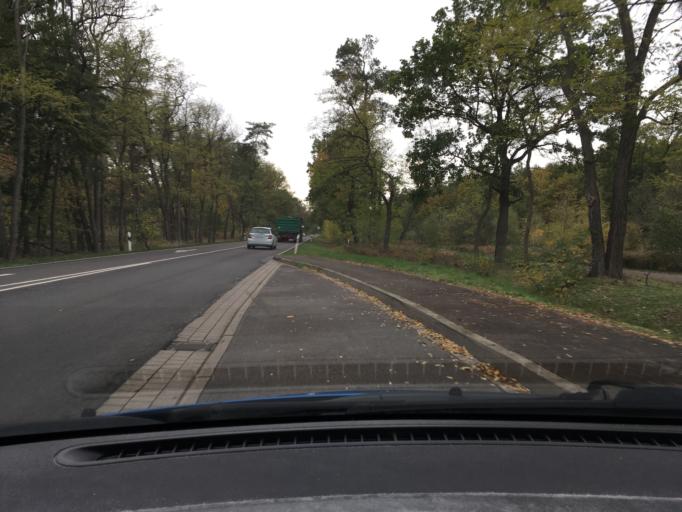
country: DE
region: Saxony-Anhalt
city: Wahlitz
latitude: 52.0896
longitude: 11.8010
